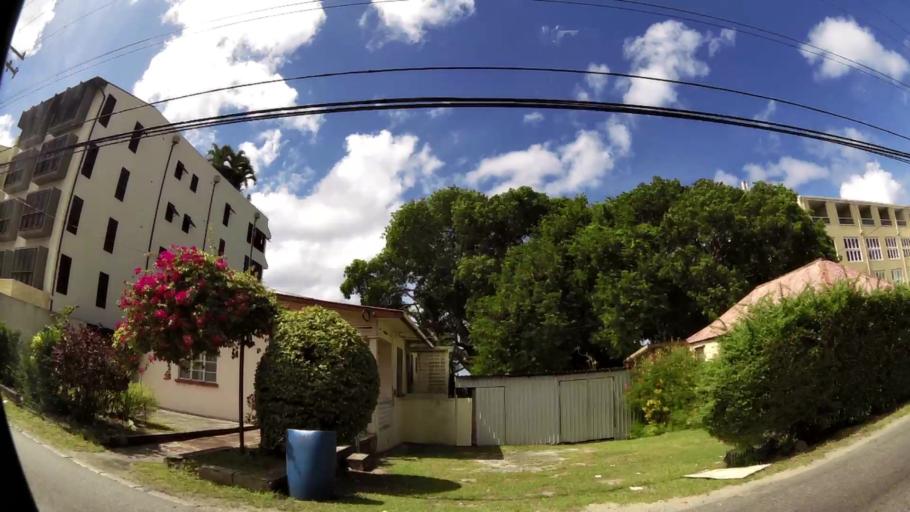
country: BB
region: Saint James
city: Holetown
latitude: 13.1417
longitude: -59.6372
